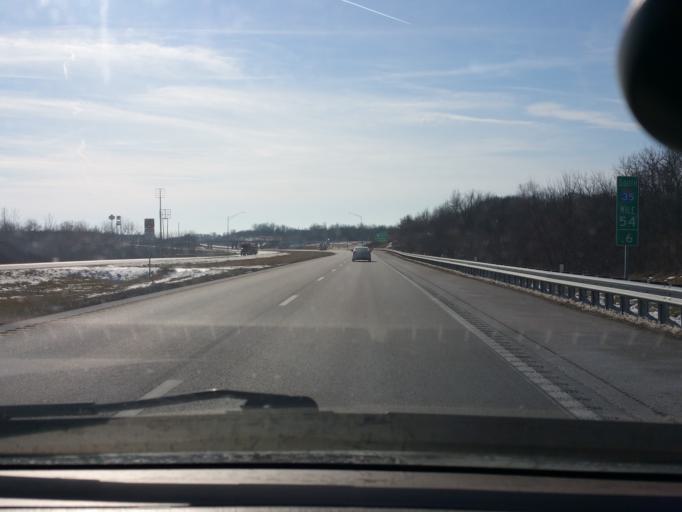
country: US
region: Missouri
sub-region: Clinton County
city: Cameron
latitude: 39.7594
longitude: -94.2187
